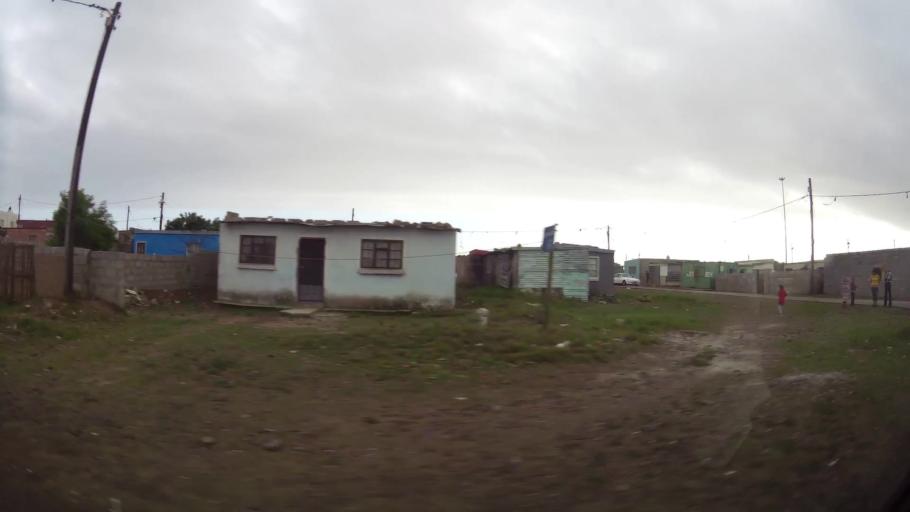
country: ZA
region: Eastern Cape
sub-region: Nelson Mandela Bay Metropolitan Municipality
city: Port Elizabeth
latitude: -33.9104
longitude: 25.5388
